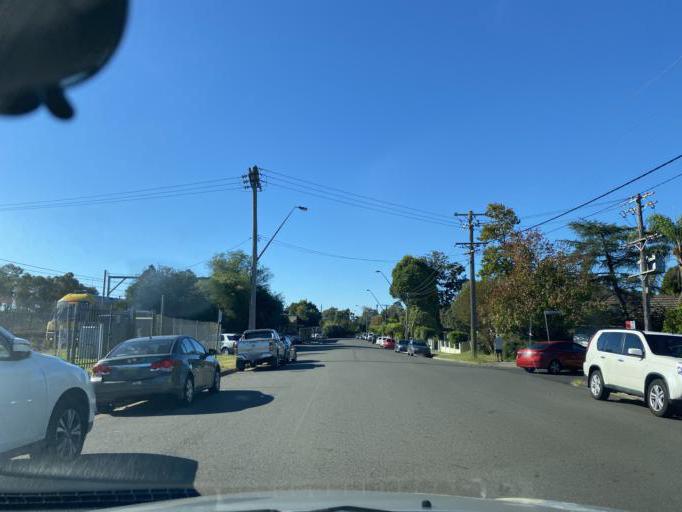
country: AU
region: New South Wales
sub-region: Campbelltown Municipality
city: Ingleburn
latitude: -33.9857
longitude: 150.8782
